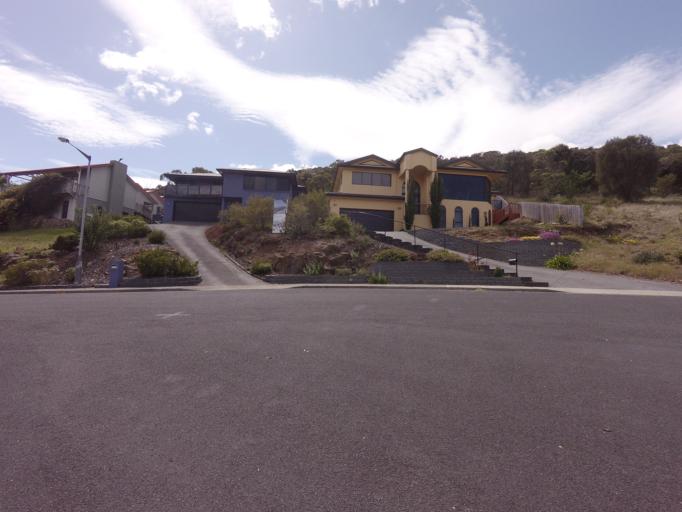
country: AU
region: Tasmania
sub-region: Clarence
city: Howrah
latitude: -42.8916
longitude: 147.4138
